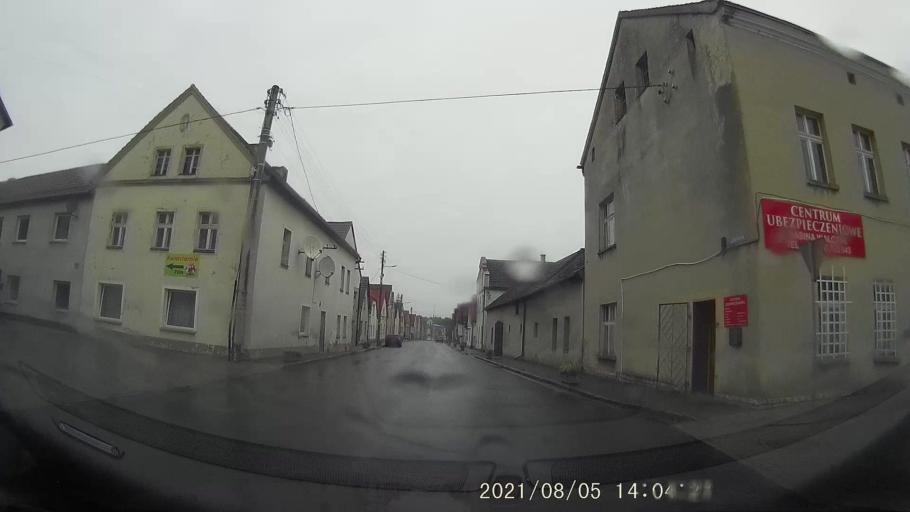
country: PL
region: Opole Voivodeship
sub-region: Powiat krapkowicki
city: Strzeleczki
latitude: 50.4600
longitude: 17.8522
